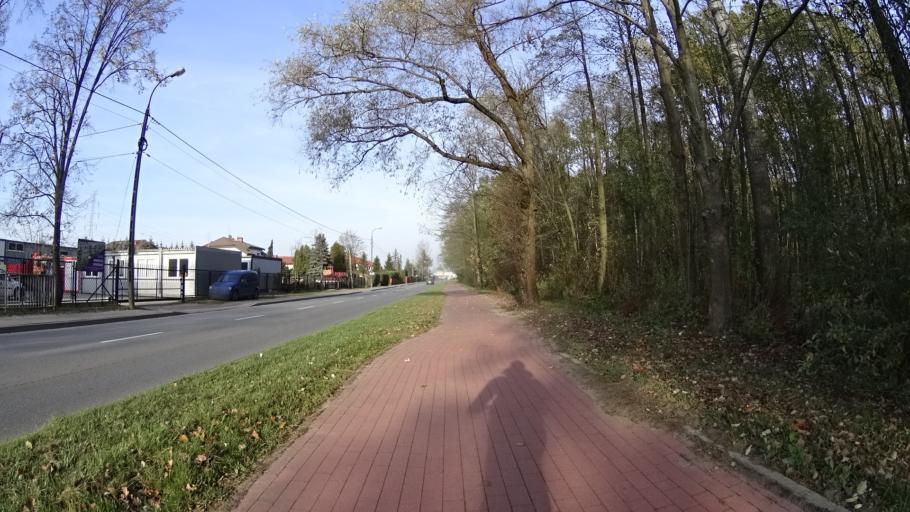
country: PL
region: Masovian Voivodeship
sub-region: Powiat warszawski zachodni
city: Babice
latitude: 52.2725
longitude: 20.8634
